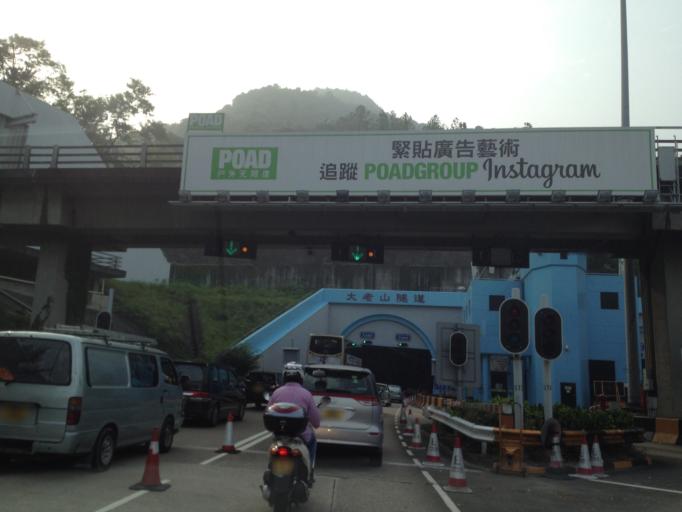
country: HK
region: Sha Tin
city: Sha Tin
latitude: 22.3766
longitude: 114.2128
